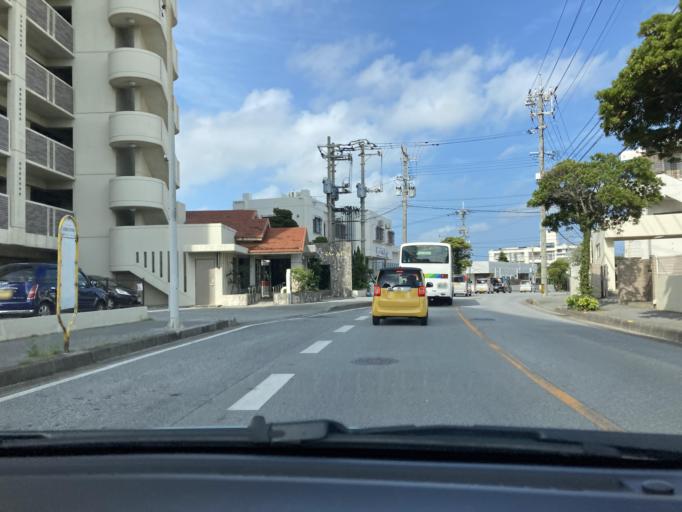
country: JP
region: Okinawa
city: Ginowan
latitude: 26.2590
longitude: 127.7658
